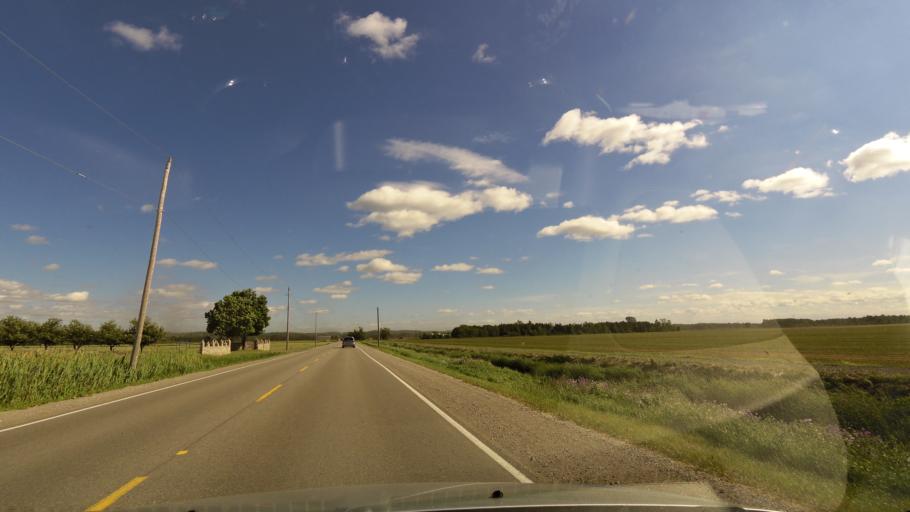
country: CA
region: Ontario
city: Innisfil
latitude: 44.2296
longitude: -79.6343
